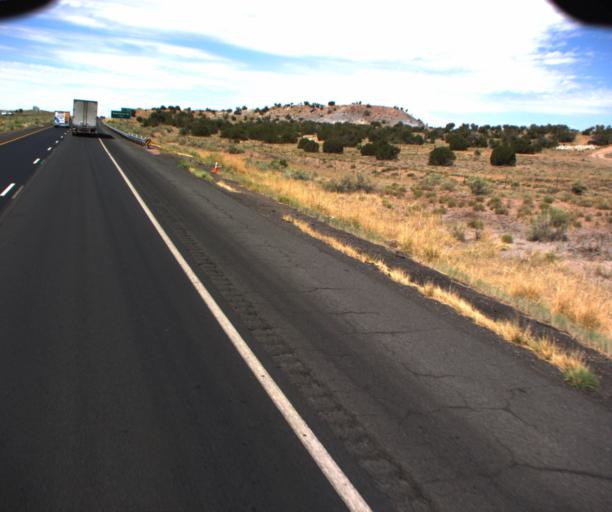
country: US
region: Arizona
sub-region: Apache County
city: Houck
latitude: 35.3207
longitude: -109.0883
